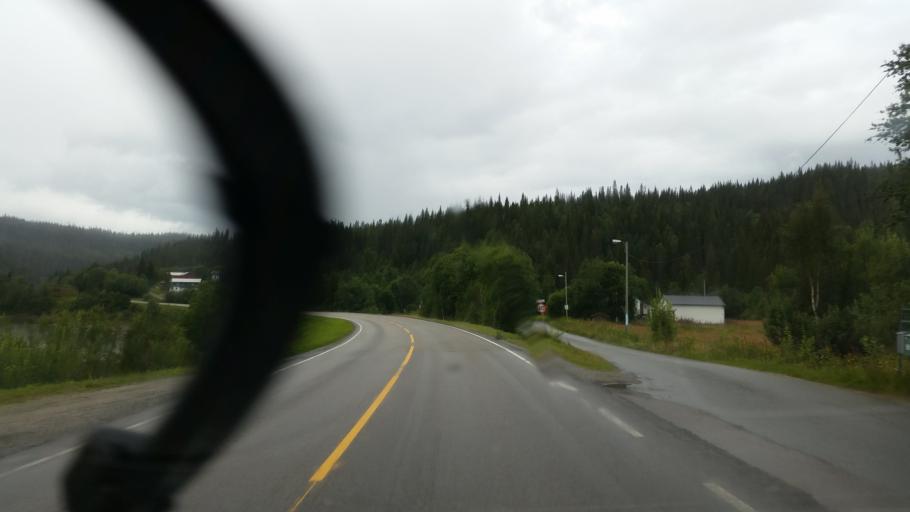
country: NO
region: Nordland
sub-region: Rana
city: Mo i Rana
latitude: 66.4065
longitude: 14.4680
